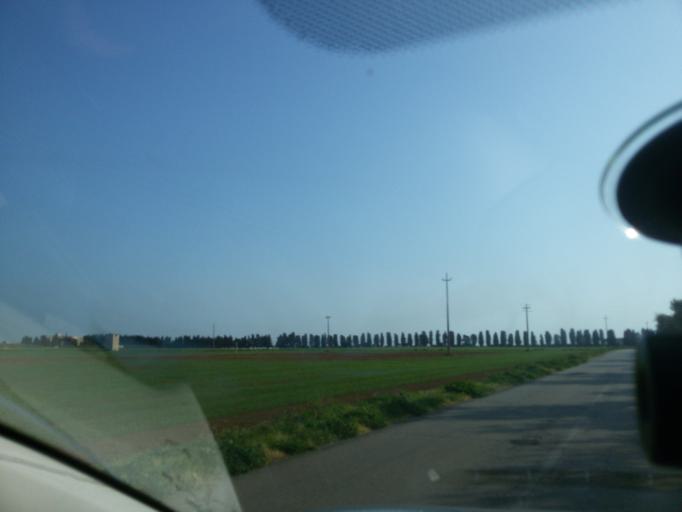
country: IT
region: Apulia
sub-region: Provincia di Brindisi
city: Mesagne
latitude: 40.6007
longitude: 17.8174
